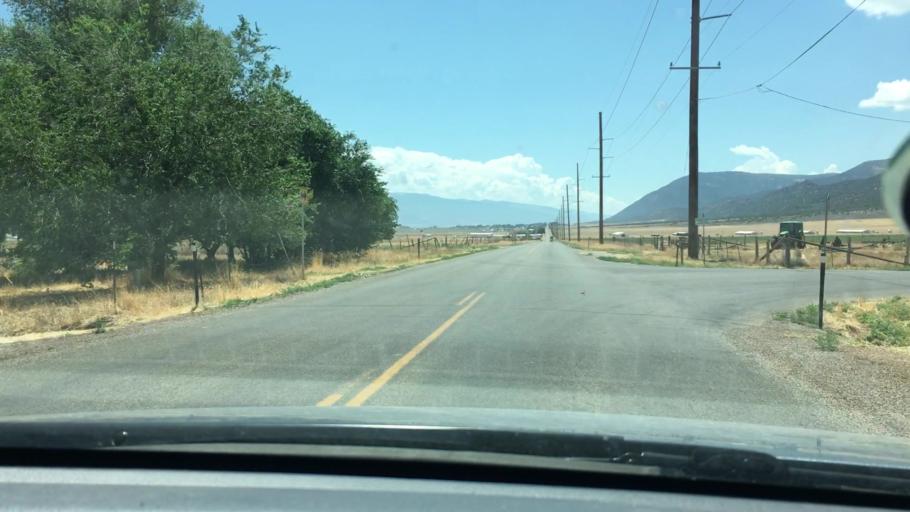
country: US
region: Utah
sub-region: Sanpete County
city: Moroni
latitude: 39.5423
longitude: -111.6400
